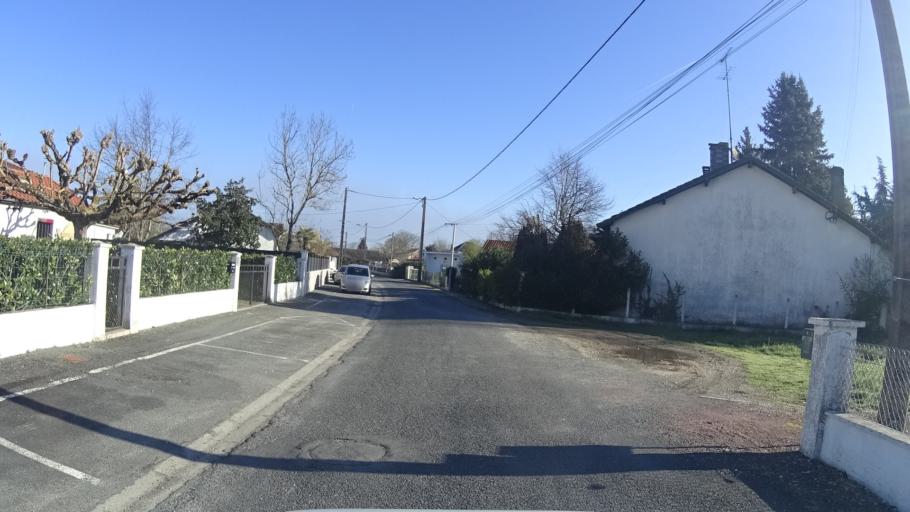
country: FR
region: Poitou-Charentes
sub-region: Departement de la Charente-Maritime
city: Saint-Aigulin
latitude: 45.1551
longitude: -0.0028
